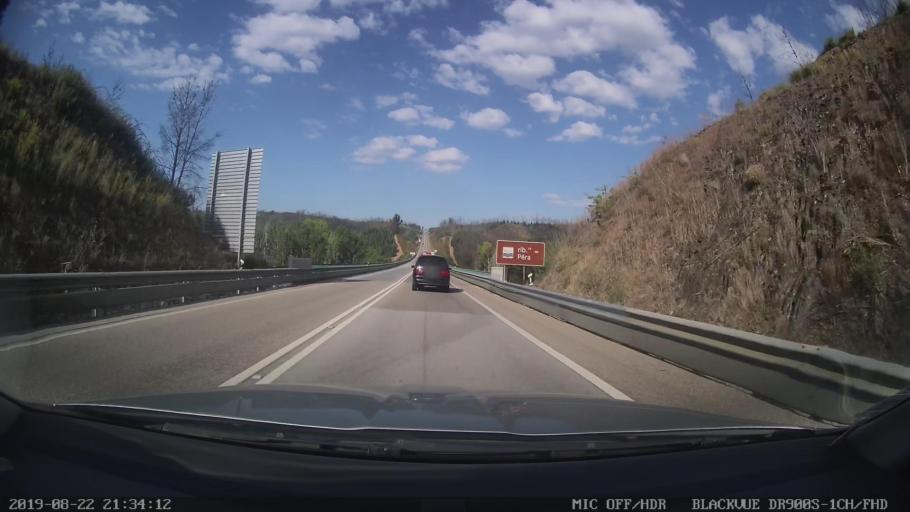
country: PT
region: Leiria
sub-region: Pedrogao Grande
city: Pedrogao Grande
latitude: 39.9277
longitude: -8.1880
